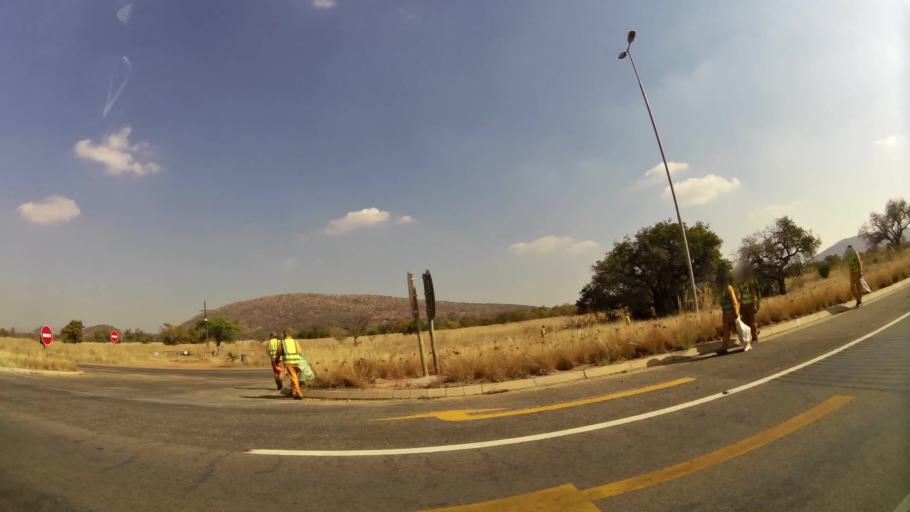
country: ZA
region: North-West
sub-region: Bojanala Platinum District Municipality
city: Rustenburg
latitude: -25.5582
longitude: 27.1425
